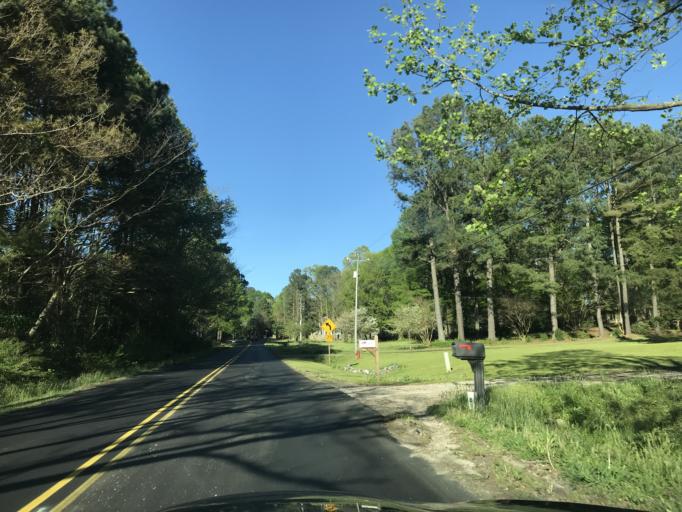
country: US
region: North Carolina
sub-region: Wake County
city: Knightdale
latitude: 35.8473
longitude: -78.5583
